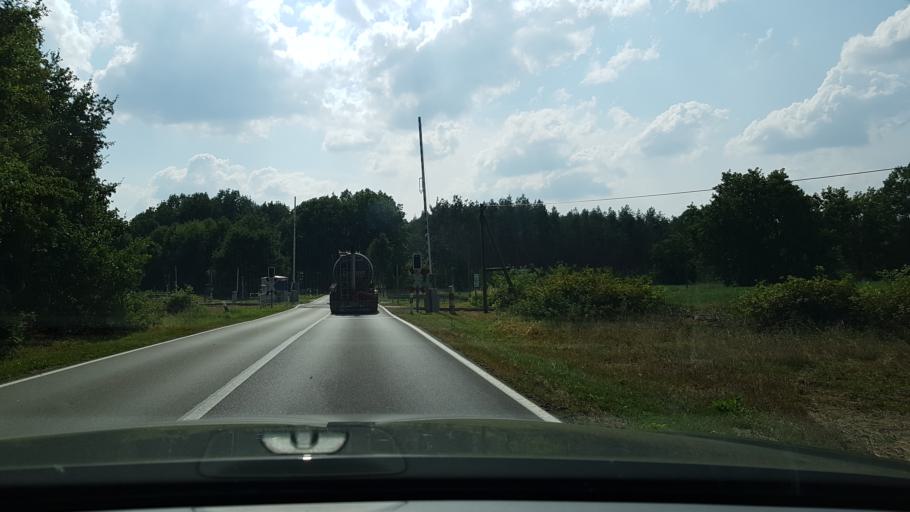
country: DE
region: Brandenburg
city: Lindow
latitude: 52.9497
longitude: 12.9764
